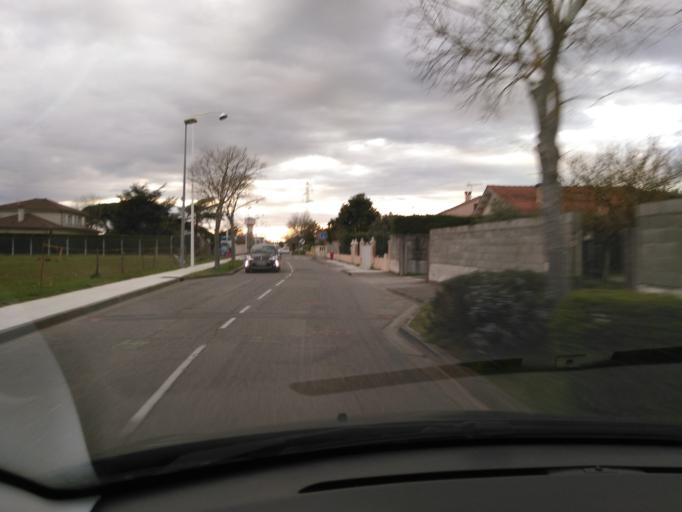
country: FR
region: Midi-Pyrenees
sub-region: Departement de la Haute-Garonne
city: La Salvetat-Saint-Gilles
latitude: 43.5748
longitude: 1.2807
